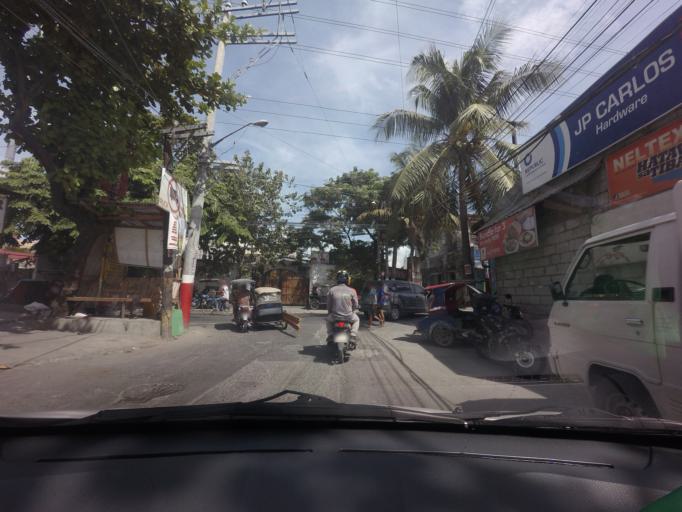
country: PH
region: Calabarzon
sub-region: Province of Rizal
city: Taguig
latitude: 14.5295
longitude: 121.0768
